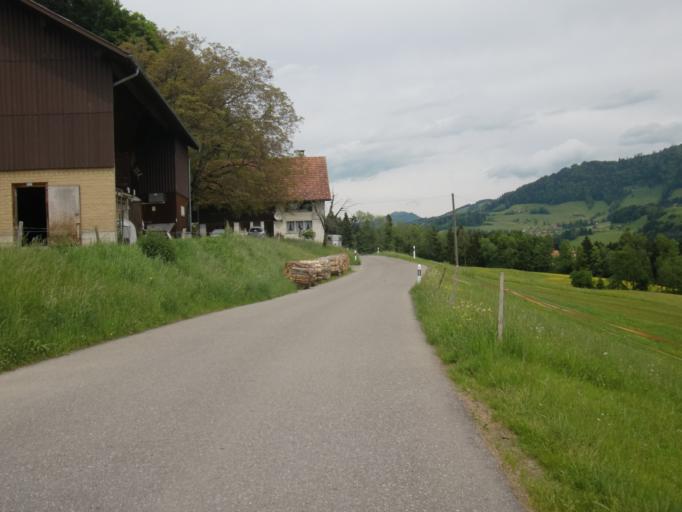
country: CH
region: Zurich
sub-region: Bezirk Hinwil
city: Wald
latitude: 47.2834
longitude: 8.9076
